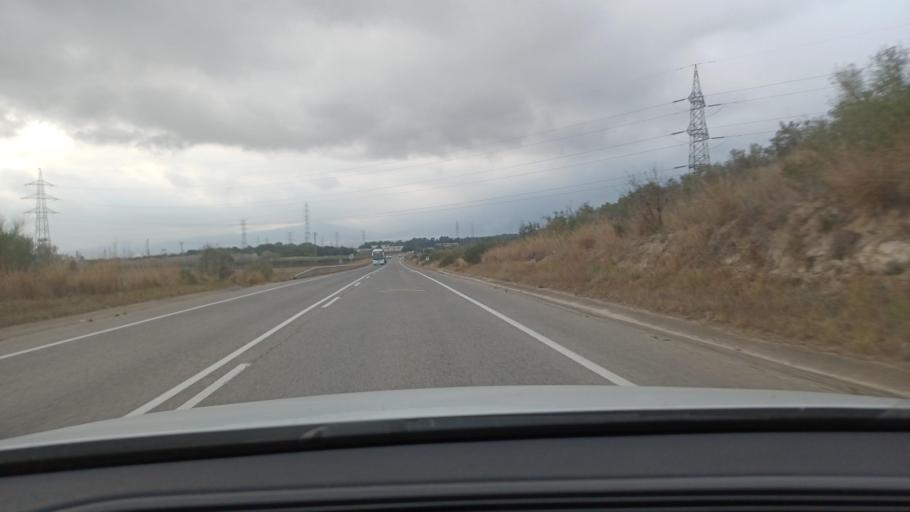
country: ES
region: Catalonia
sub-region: Provincia de Tarragona
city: La Secuita
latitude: 41.1976
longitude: 1.2559
